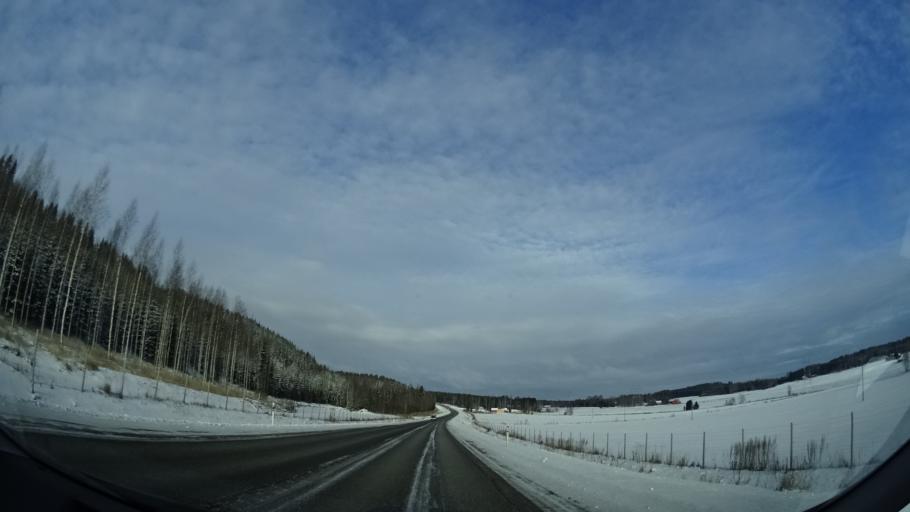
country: FI
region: Uusimaa
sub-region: Helsinki
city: Karkkila
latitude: 60.5804
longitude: 24.1332
